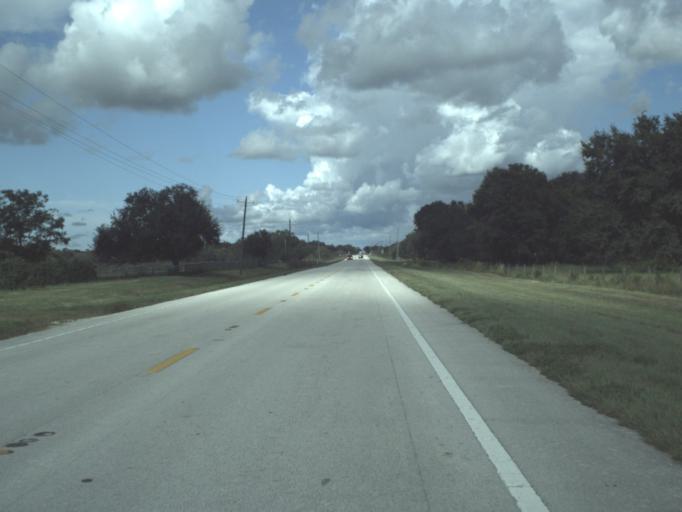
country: US
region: Florida
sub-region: DeSoto County
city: Arcadia
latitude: 27.2529
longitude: -81.9621
